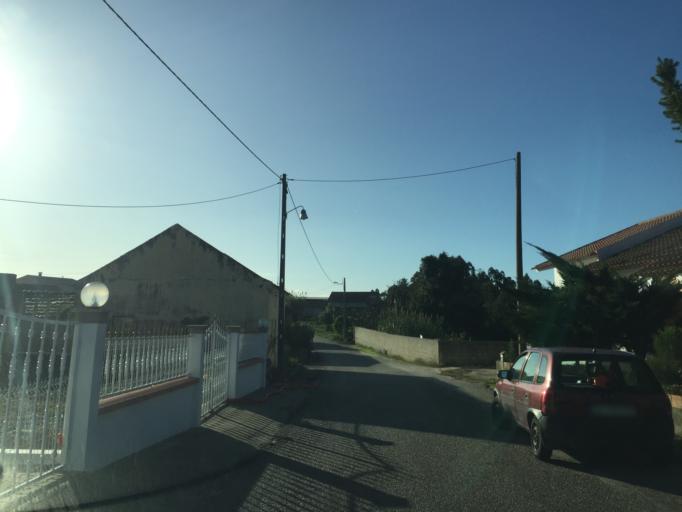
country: PT
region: Coimbra
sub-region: Figueira da Foz
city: Lavos
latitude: 40.0523
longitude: -8.7917
